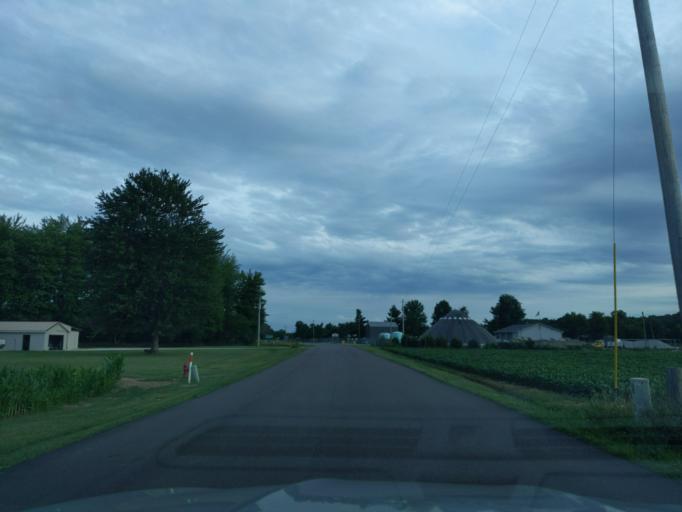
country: US
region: Indiana
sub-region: Ripley County
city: Sunman
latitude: 39.2854
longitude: -85.1012
